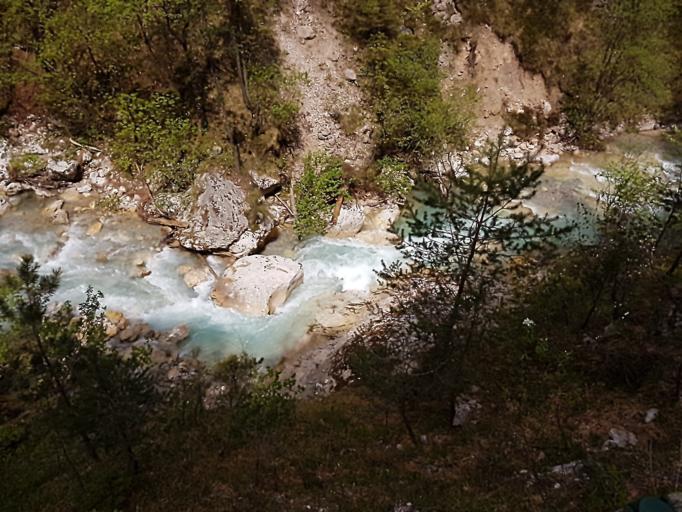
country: AT
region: Carinthia
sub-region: Politischer Bezirk Klagenfurt Land
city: Ferlach
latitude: 46.4860
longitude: 14.2711
